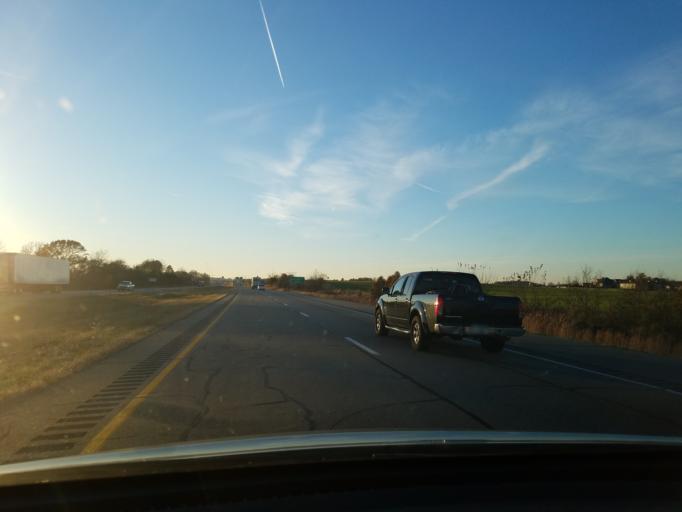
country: US
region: Indiana
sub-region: Gibson County
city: Haubstadt
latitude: 38.1672
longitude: -87.5348
